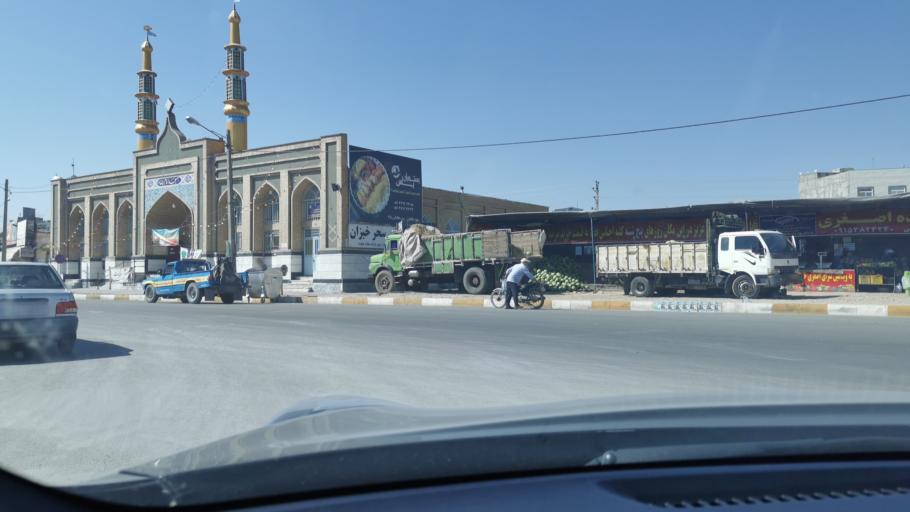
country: IR
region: Razavi Khorasan
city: Chenaran
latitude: 36.6409
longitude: 59.1174
